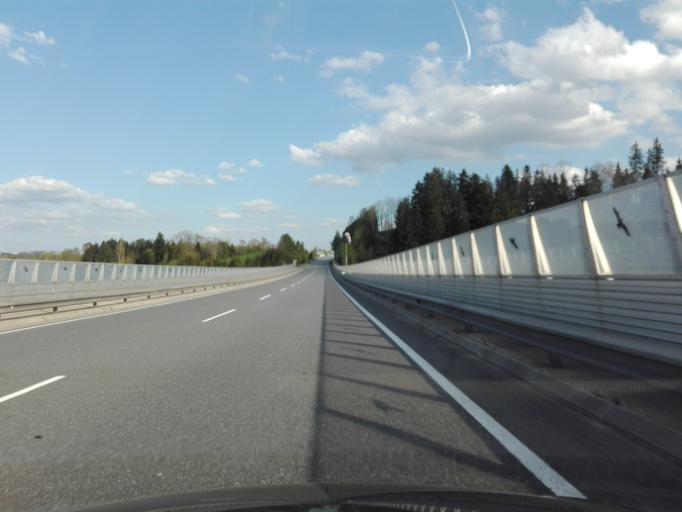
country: AT
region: Upper Austria
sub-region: Politischer Bezirk Rohrbach
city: Kleinzell im Muehlkreis
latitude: 48.4772
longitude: 13.9948
